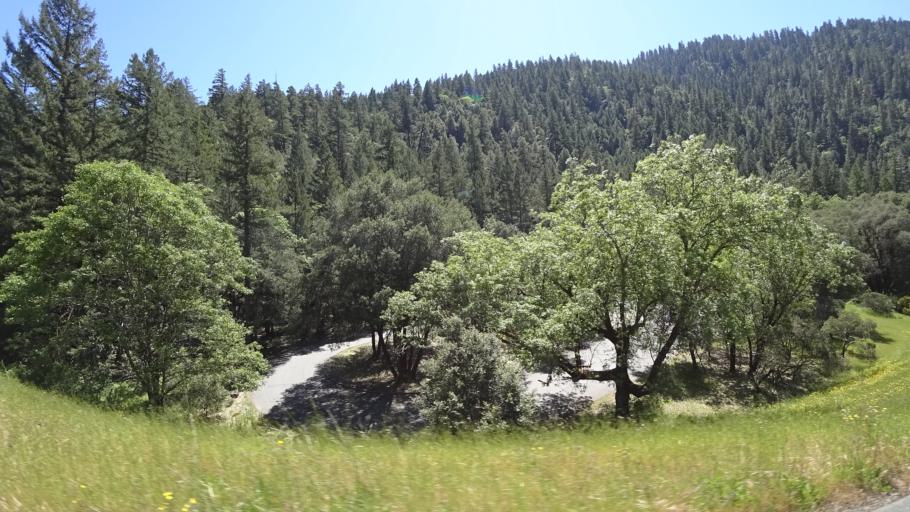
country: US
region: California
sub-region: Humboldt County
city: Willow Creek
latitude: 40.8835
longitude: -123.5472
